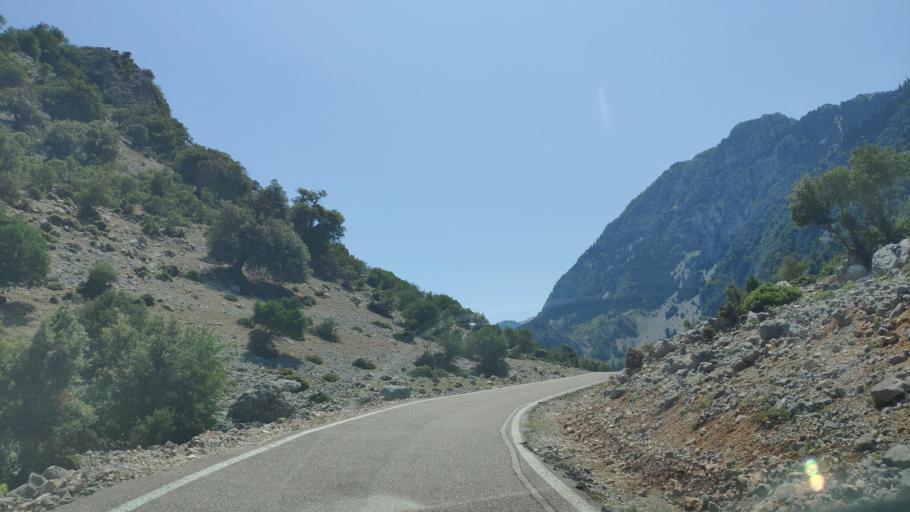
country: GR
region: West Greece
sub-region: Nomos Aitolias kai Akarnanias
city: Krikellos
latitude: 39.0106
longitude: 21.3592
